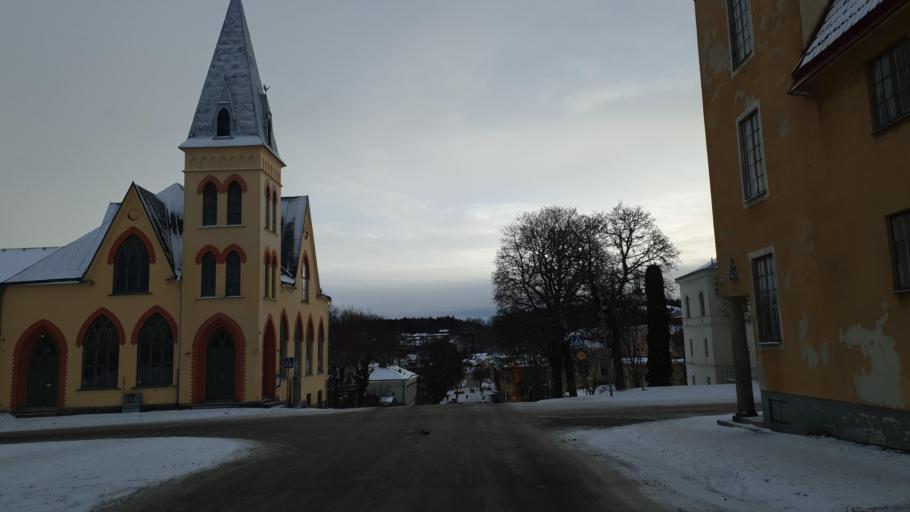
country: SE
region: Gaevleborg
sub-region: Soderhamns Kommun
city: Soderhamn
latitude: 61.3052
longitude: 17.0551
